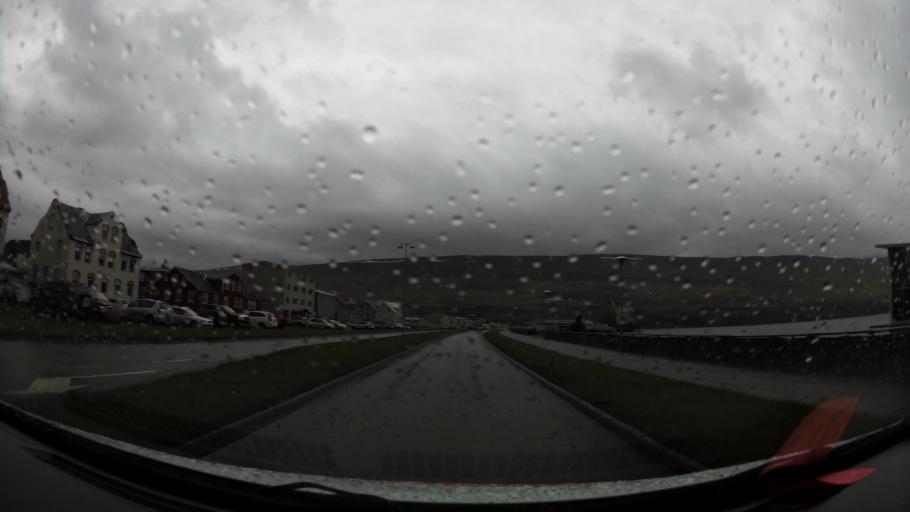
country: IS
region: Northeast
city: Akureyri
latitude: 65.6843
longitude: -18.0861
